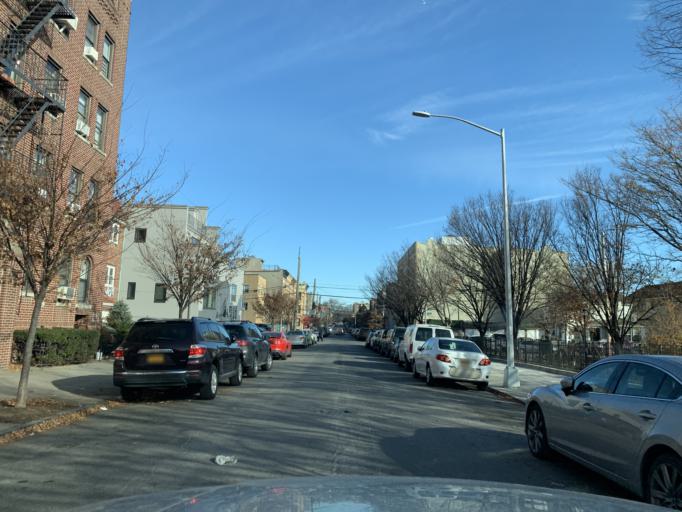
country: US
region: New York
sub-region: Queens County
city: Long Island City
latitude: 40.7609
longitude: -73.9119
